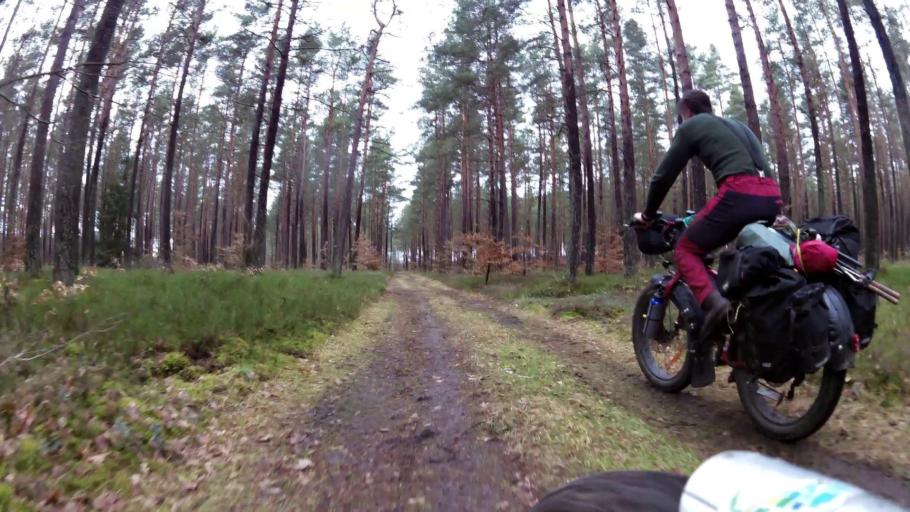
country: PL
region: Pomeranian Voivodeship
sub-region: Powiat bytowski
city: Kolczyglowy
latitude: 54.2395
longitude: 17.2530
